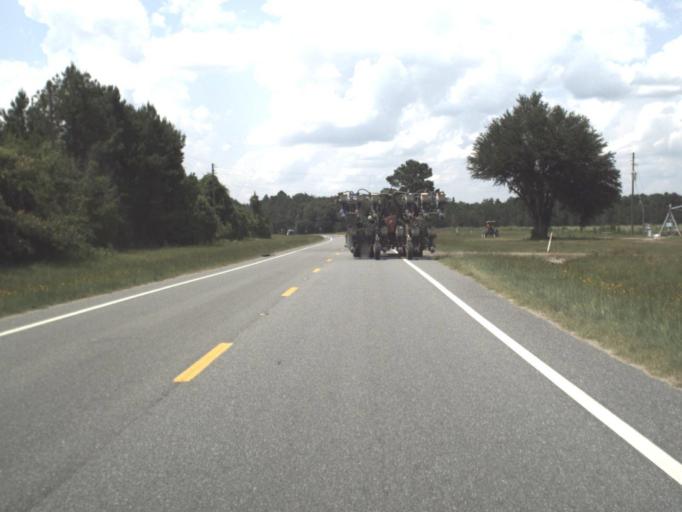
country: US
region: Georgia
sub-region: Echols County
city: Statenville
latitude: 30.5912
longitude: -83.0933
